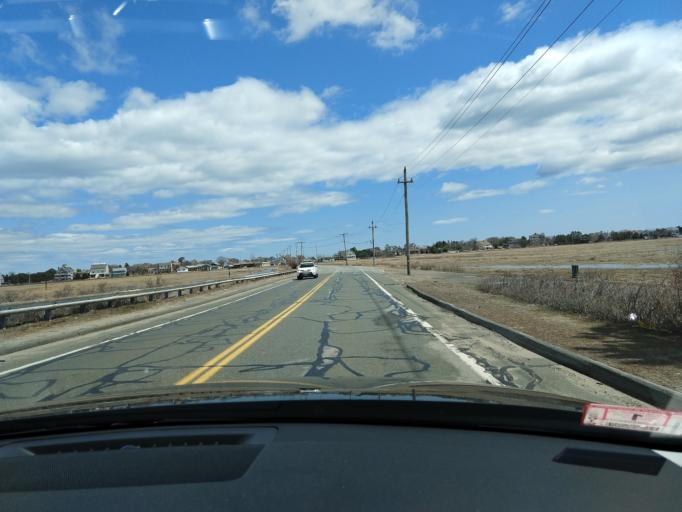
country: US
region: Massachusetts
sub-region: Essex County
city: Newburyport
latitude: 42.7981
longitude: -70.8186
